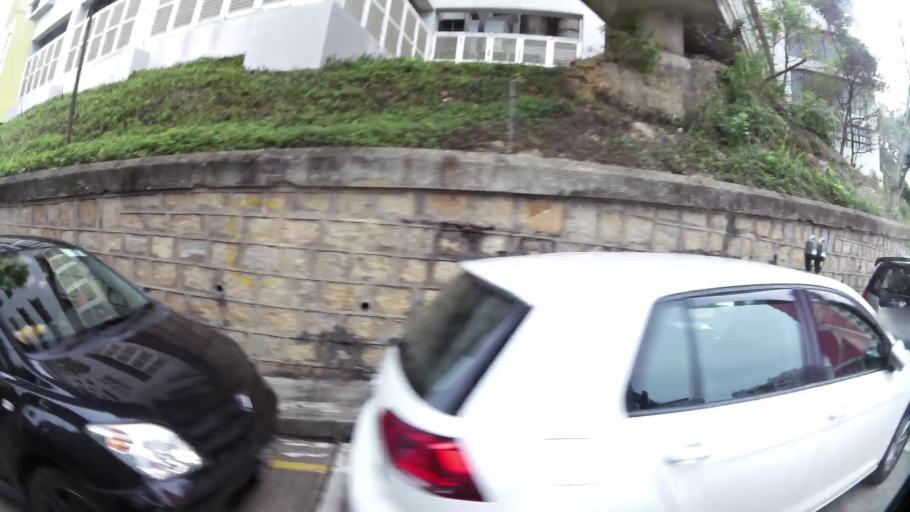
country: MO
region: Macau
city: Macau
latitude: 22.1643
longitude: 113.5593
